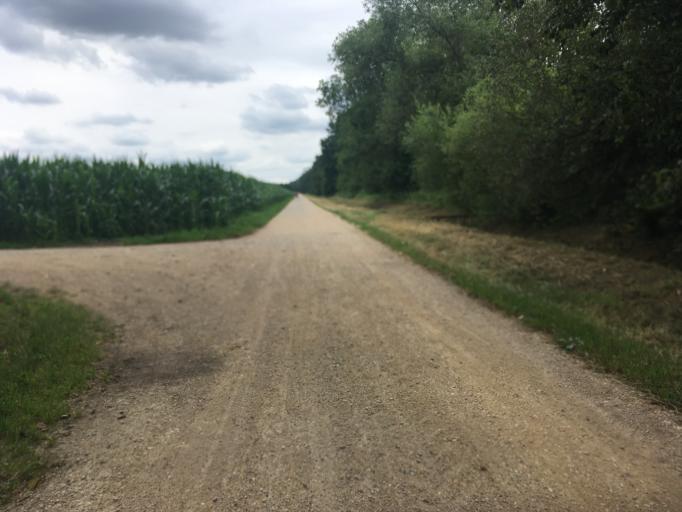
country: CH
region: Vaud
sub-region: Broye-Vully District
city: Avenches
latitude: 46.8982
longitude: 7.0349
